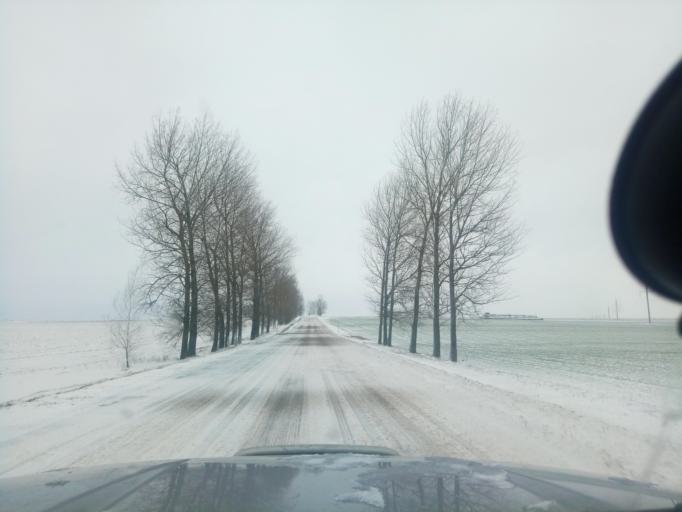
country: BY
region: Minsk
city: Tsimkavichy
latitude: 53.0545
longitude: 26.9414
